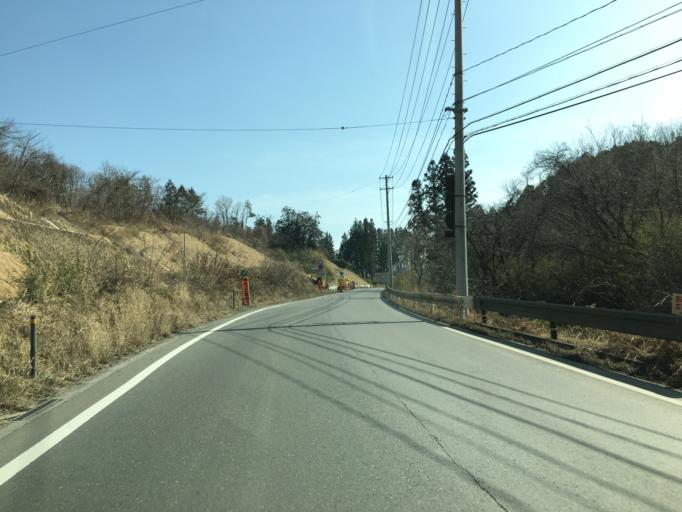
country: JP
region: Ibaraki
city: Daigo
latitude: 36.8494
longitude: 140.4322
